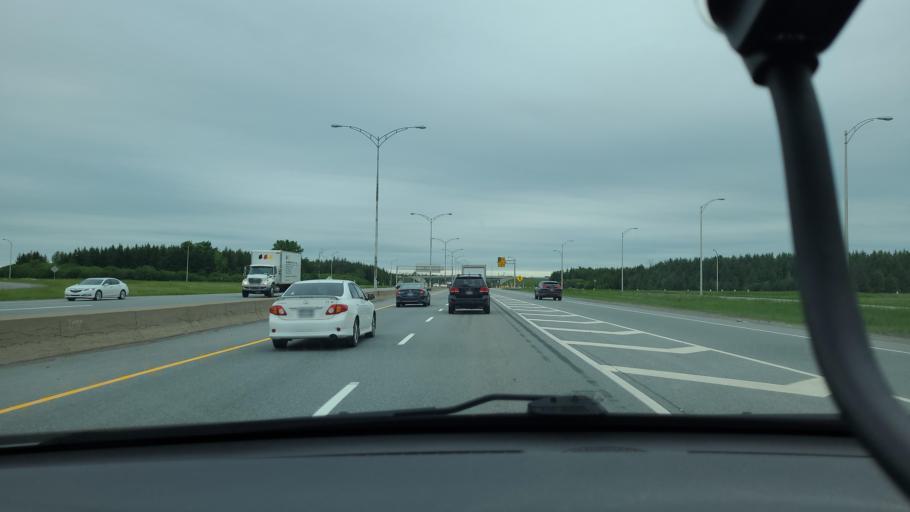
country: CA
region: Quebec
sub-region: Laval
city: Laval
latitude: 45.6249
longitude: -73.6612
